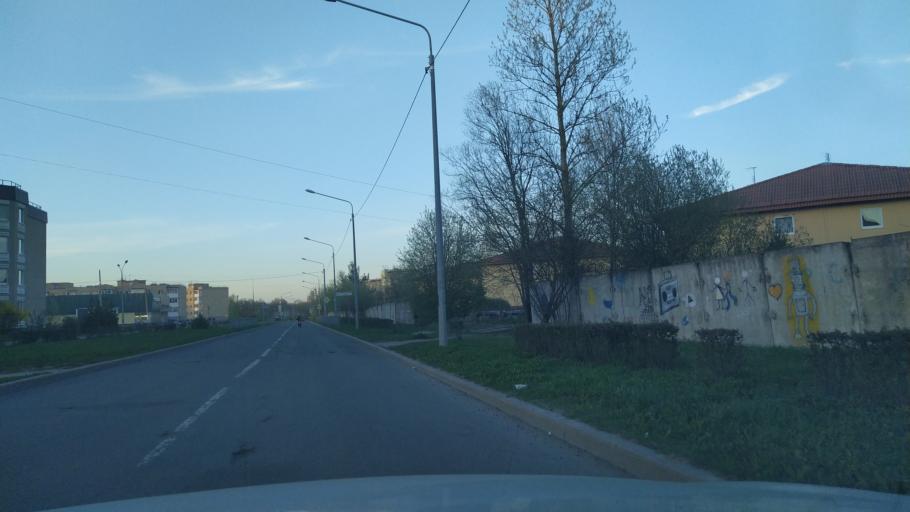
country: RU
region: St.-Petersburg
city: Pushkin
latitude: 59.7021
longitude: 30.3830
